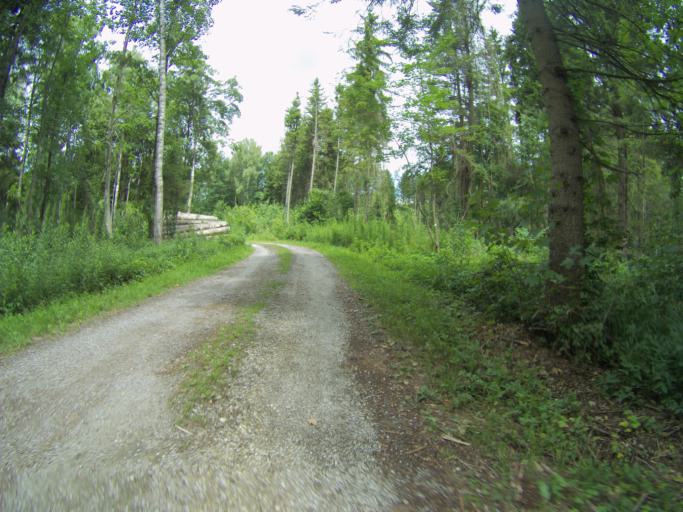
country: DE
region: Bavaria
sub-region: Upper Bavaria
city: Freising
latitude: 48.3762
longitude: 11.7399
